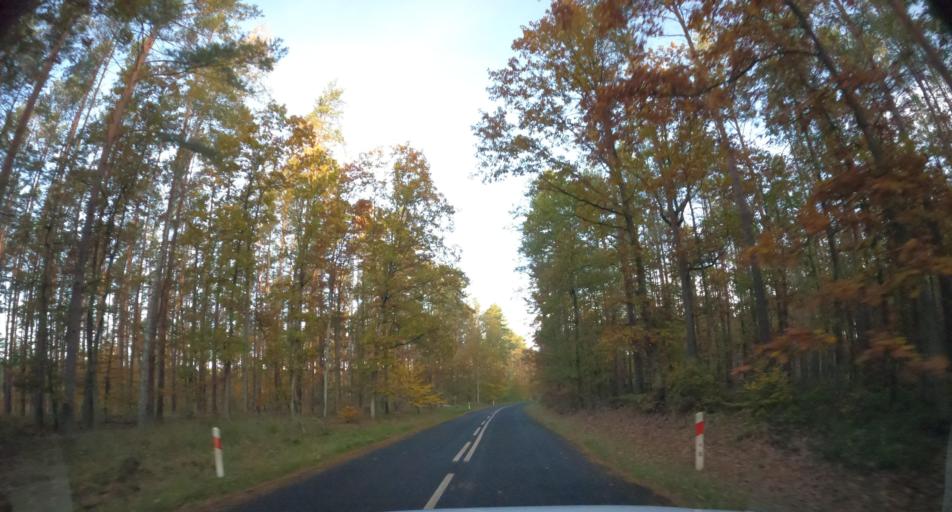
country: PL
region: West Pomeranian Voivodeship
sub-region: Powiat policki
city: Nowe Warpno
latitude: 53.6066
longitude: 14.3182
